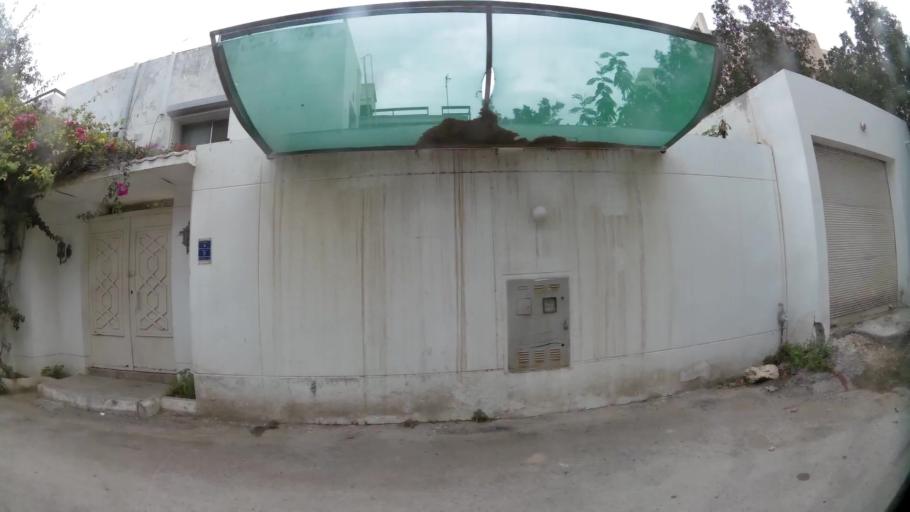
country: QA
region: Baladiyat ad Dawhah
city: Doha
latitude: 25.2760
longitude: 51.5033
